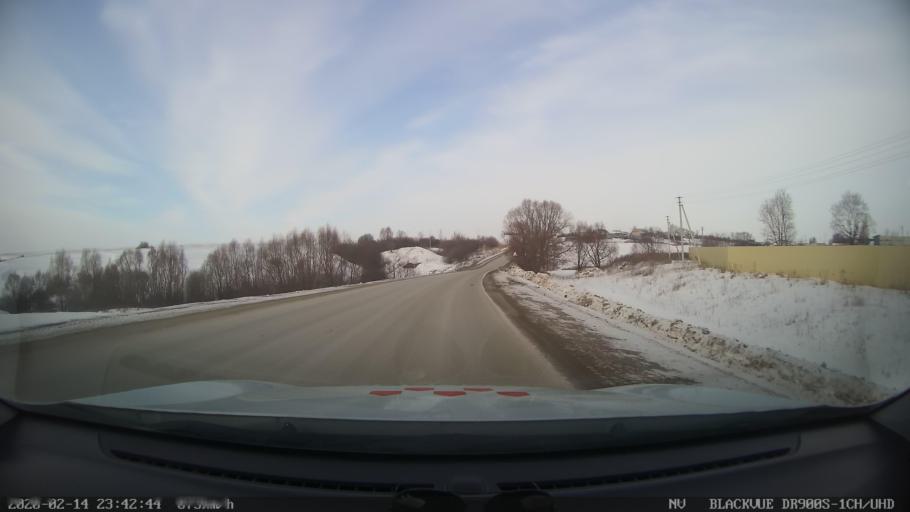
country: RU
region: Tatarstan
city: Kuybyshevskiy Zaton
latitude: 55.1942
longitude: 49.2471
